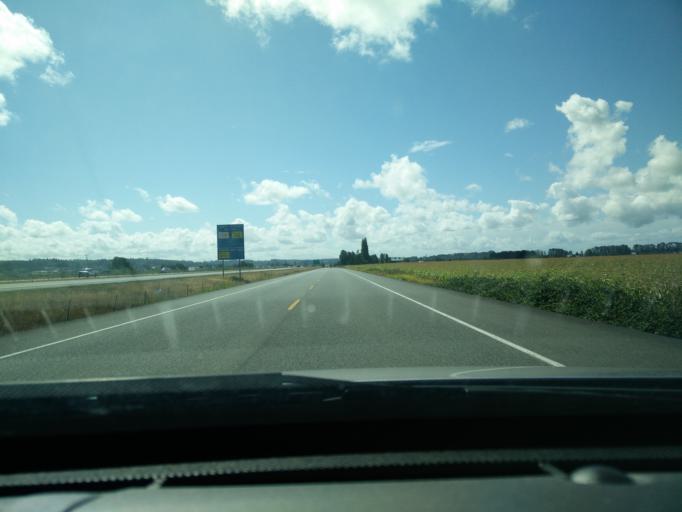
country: US
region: Washington
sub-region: Skagit County
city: Mount Vernon
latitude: 48.3646
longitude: -122.3364
